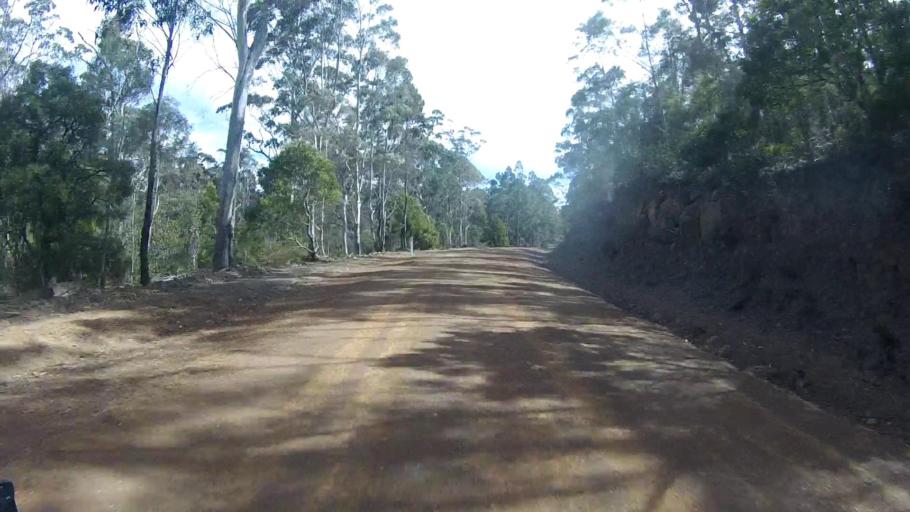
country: AU
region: Tasmania
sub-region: Sorell
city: Sorell
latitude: -42.6119
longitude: 147.8979
